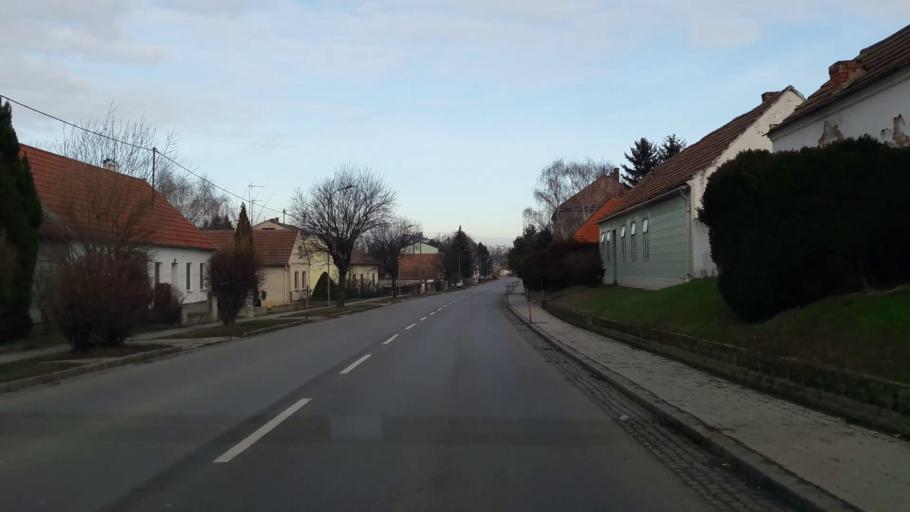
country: AT
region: Lower Austria
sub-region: Politischer Bezirk Mistelbach
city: Staatz
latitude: 48.6588
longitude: 16.4961
